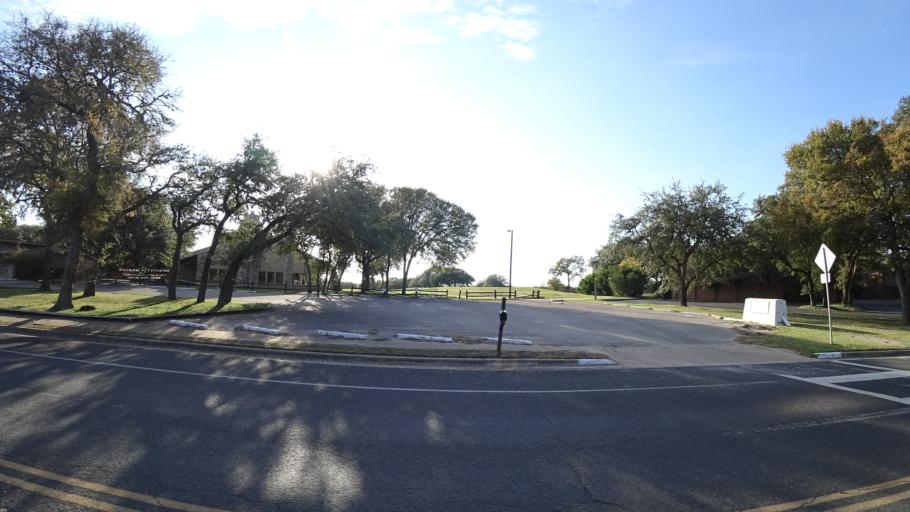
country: US
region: Texas
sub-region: Williamson County
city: Anderson Mill
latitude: 30.4406
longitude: -97.8064
